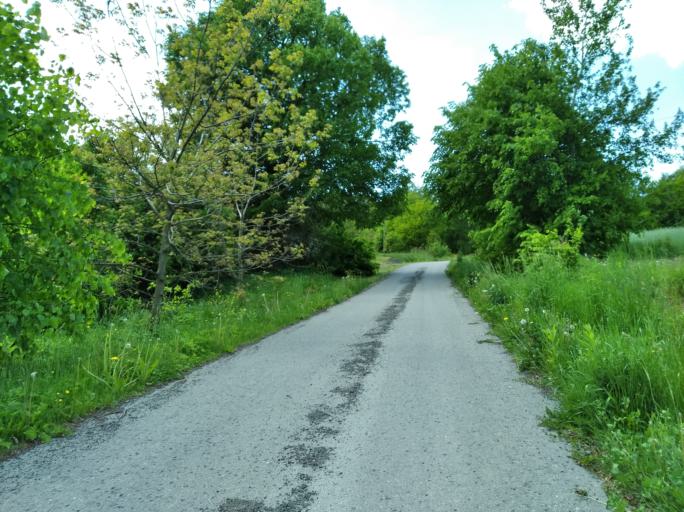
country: PL
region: Subcarpathian Voivodeship
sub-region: Powiat ropczycko-sedziszowski
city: Wielopole Skrzynskie
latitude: 49.9224
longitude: 21.6198
